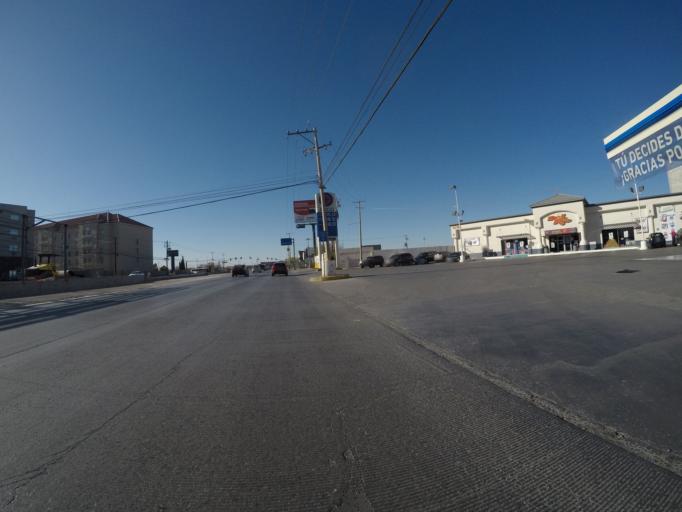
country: MX
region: Chihuahua
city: Ciudad Juarez
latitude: 31.6922
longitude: -106.4247
